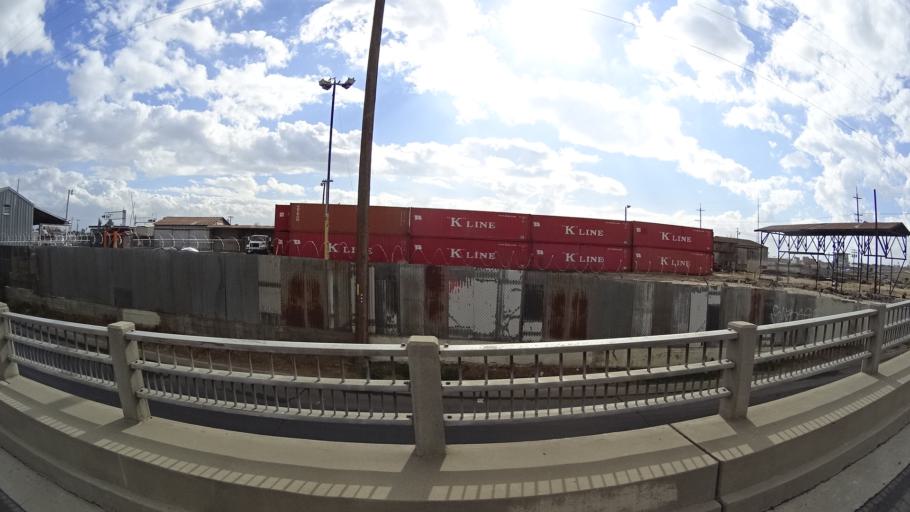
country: US
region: California
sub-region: Kern County
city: Bakersfield
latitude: 35.3732
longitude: -119.0020
